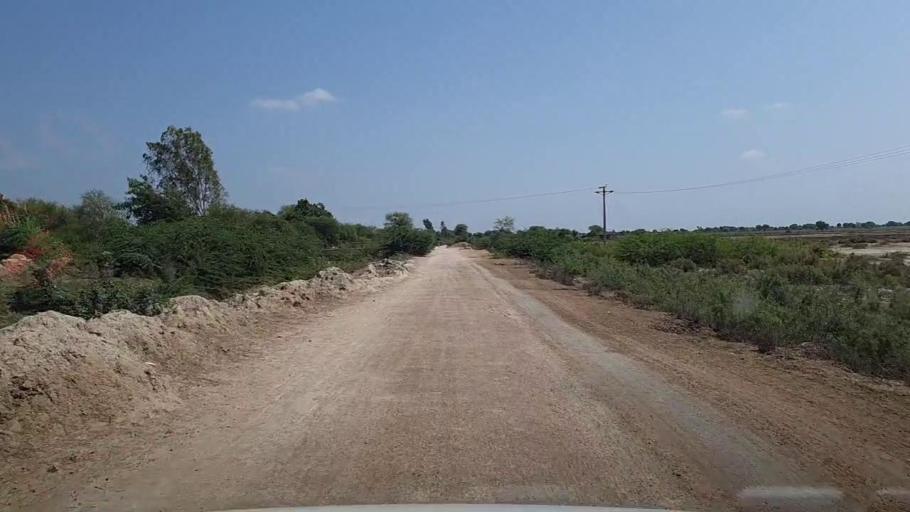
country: PK
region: Sindh
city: Kario
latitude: 24.8421
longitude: 68.7019
